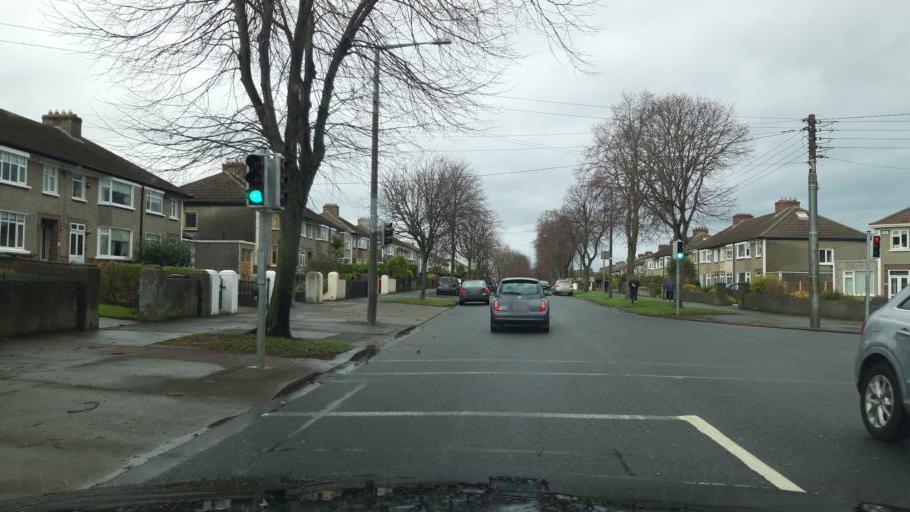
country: IE
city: Killester
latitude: 53.3772
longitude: -6.1961
